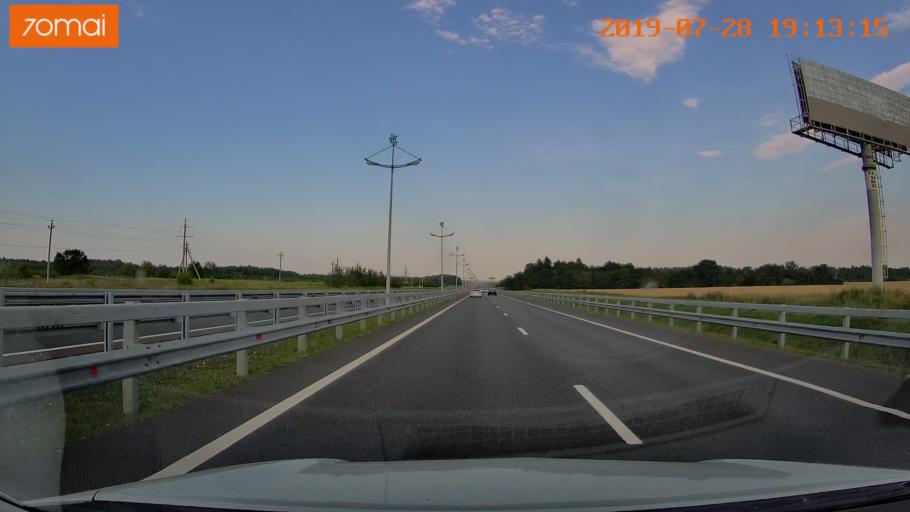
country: RU
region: Kaliningrad
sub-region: Gorod Kaliningrad
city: Pionerskiy
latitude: 54.9209
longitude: 20.2840
